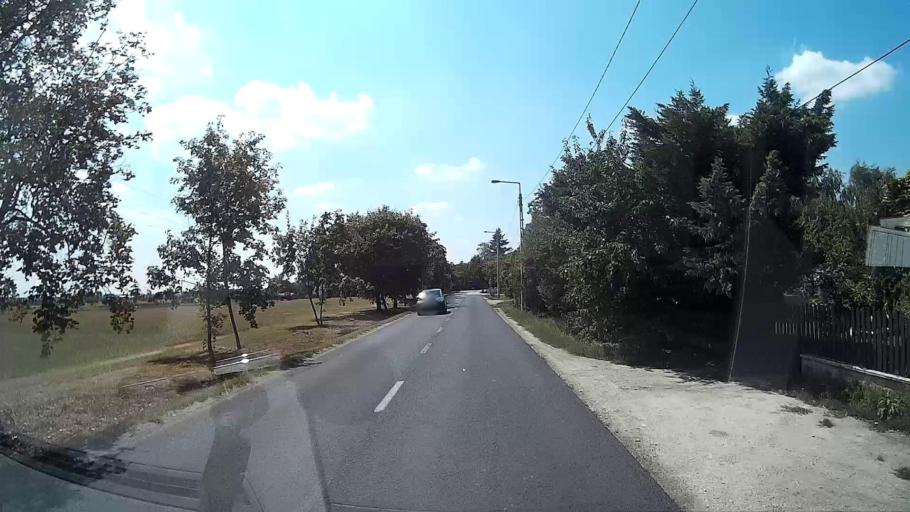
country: HU
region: Pest
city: Budakalasz
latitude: 47.6307
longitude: 19.0594
